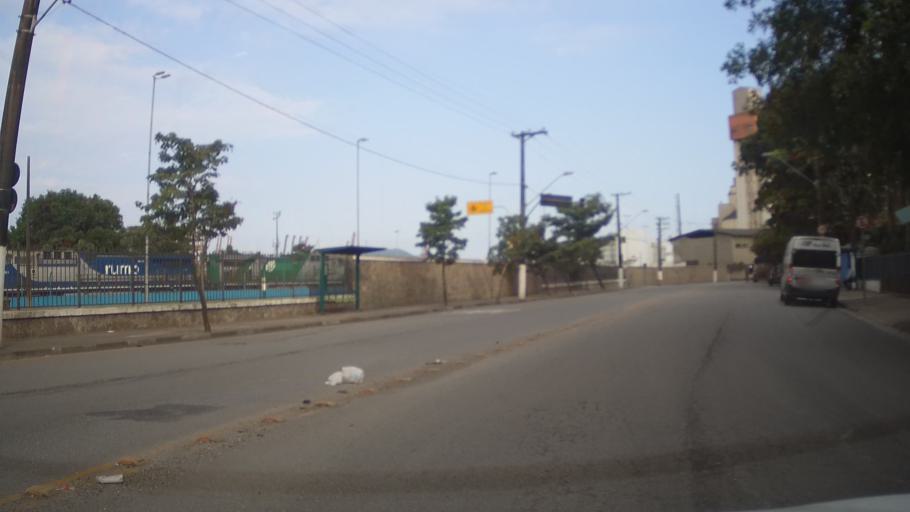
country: BR
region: Sao Paulo
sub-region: Santos
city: Santos
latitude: -23.9569
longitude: -46.3096
